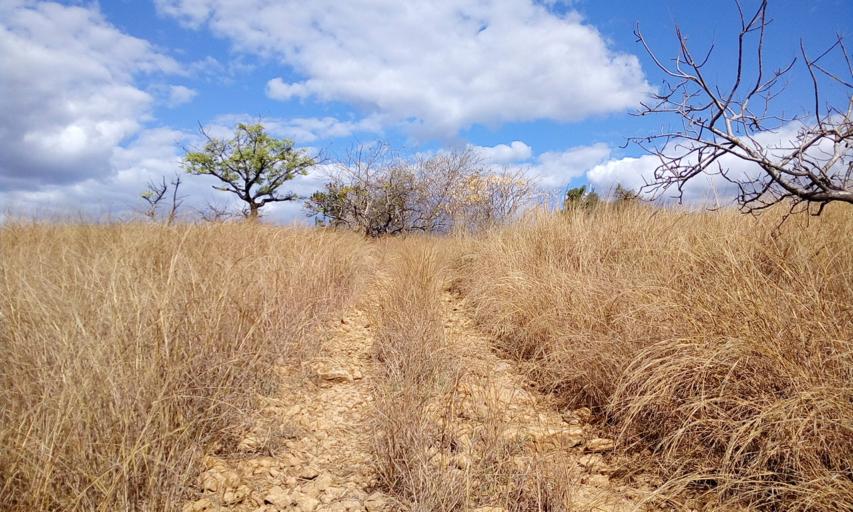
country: MG
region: Melaky
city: Mahabe
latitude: -16.3823
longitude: 45.3435
